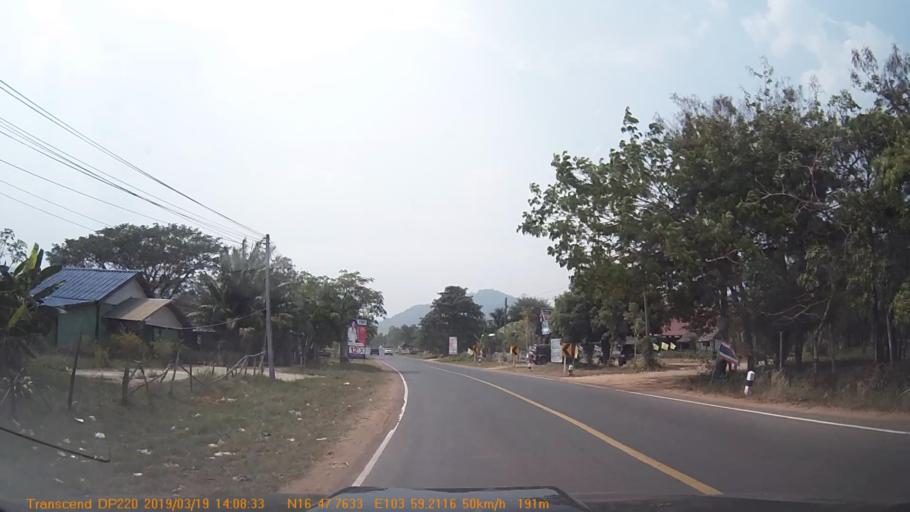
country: TH
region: Kalasin
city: Na Khu
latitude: 16.7963
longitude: 103.9865
